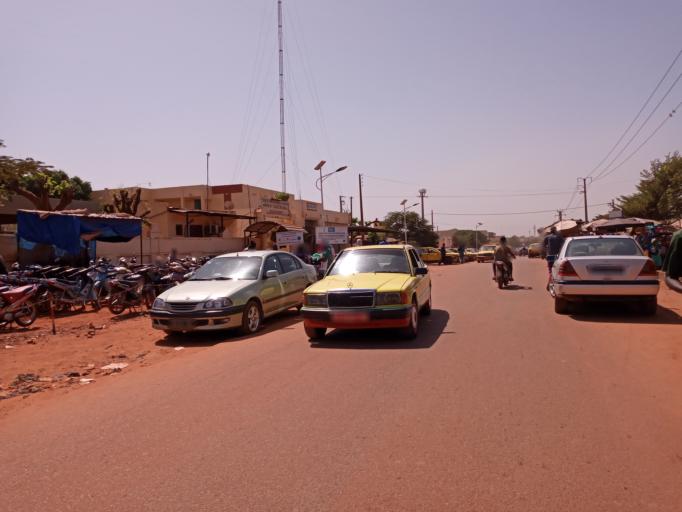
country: ML
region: Bamako
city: Bamako
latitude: 12.6121
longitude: -7.9953
